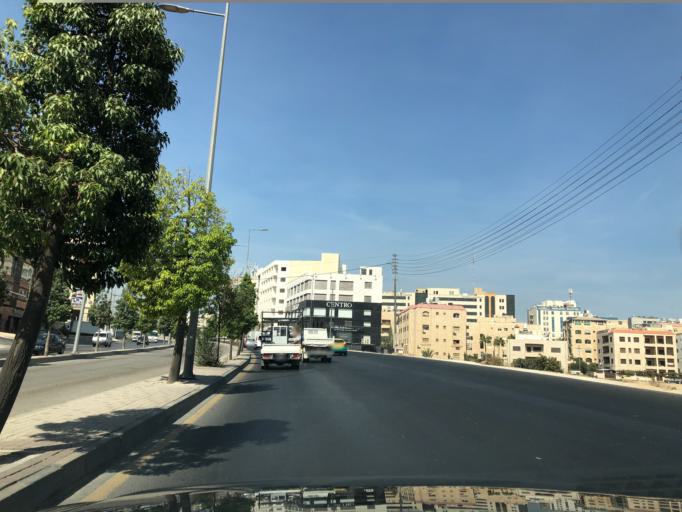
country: JO
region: Amman
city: Al Jubayhah
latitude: 32.0239
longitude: 35.8586
